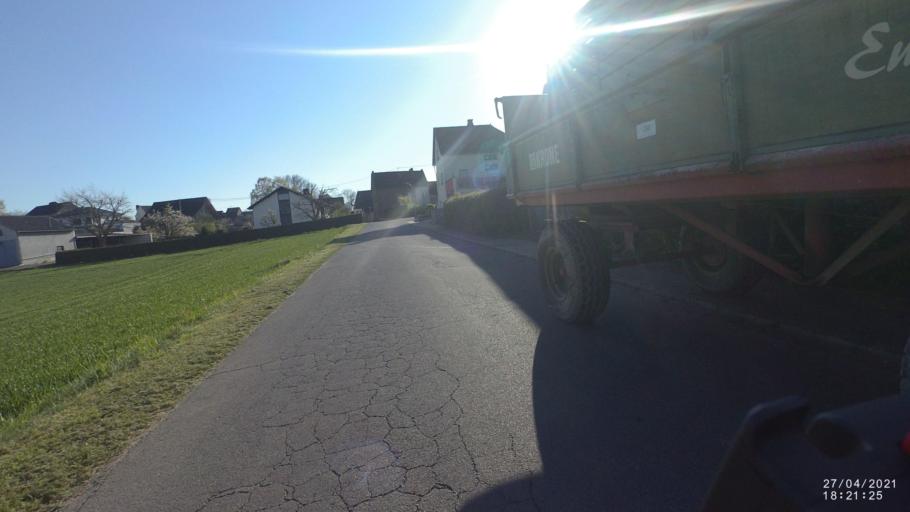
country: DE
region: Rheinland-Pfalz
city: Einig
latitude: 50.2817
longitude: 7.2798
